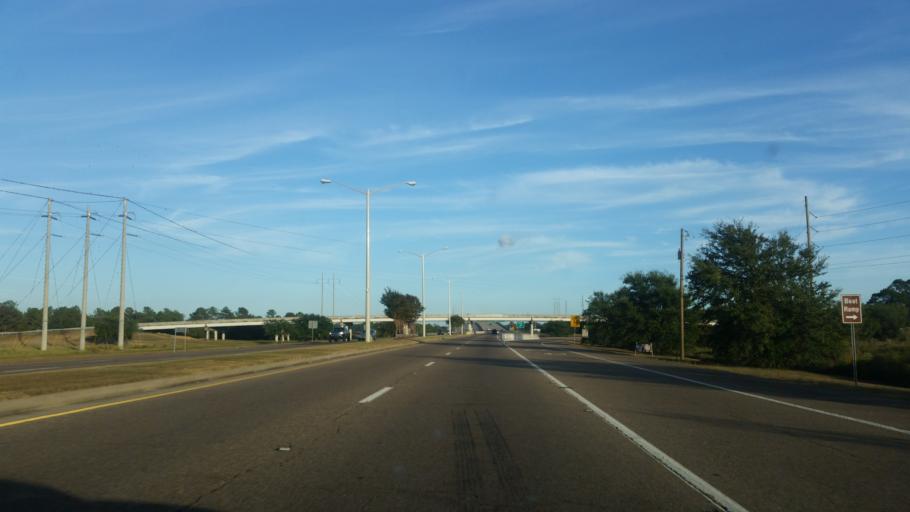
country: US
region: Mississippi
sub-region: Jackson County
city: Pascagoula
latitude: 30.3748
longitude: -88.5738
